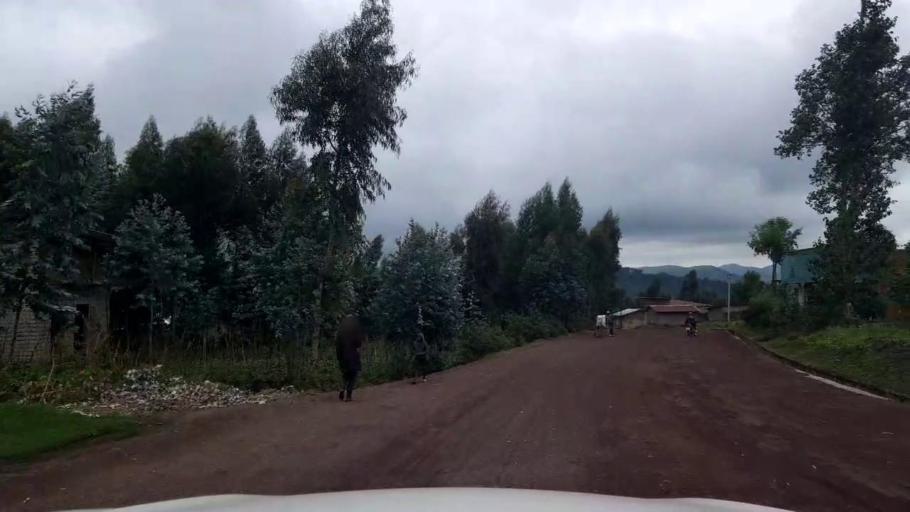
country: RW
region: Northern Province
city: Musanze
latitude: -1.6003
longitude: 29.4525
